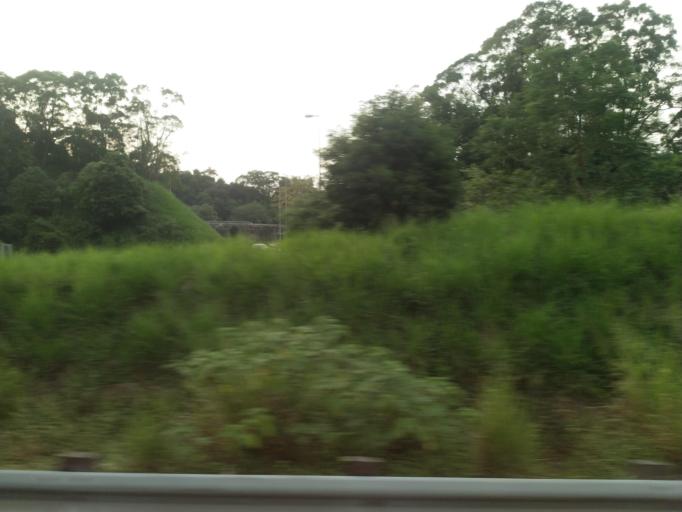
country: TW
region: Taiwan
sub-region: Pingtung
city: Pingtung
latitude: 22.7874
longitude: 120.4276
